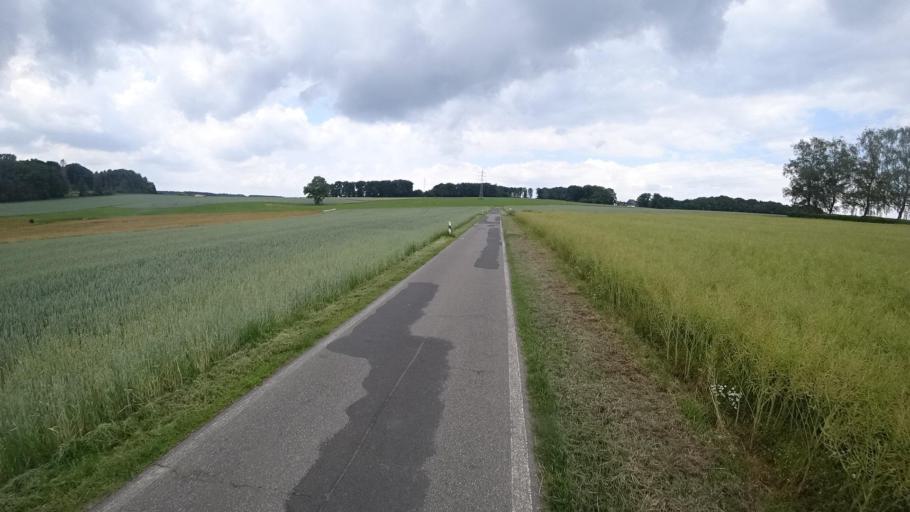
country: DE
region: Rheinland-Pfalz
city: Bachenberg
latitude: 50.7072
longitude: 7.6479
